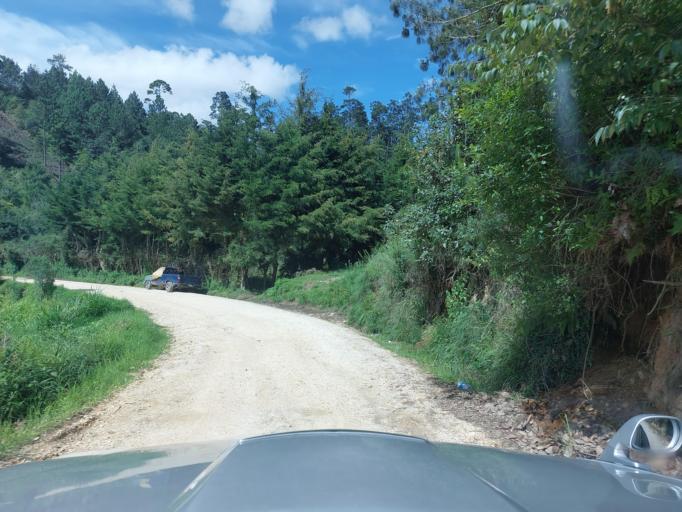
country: GT
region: Chimaltenango
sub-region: Municipio de San Juan Comalapa
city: Comalapa
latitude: 14.7551
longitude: -90.8728
